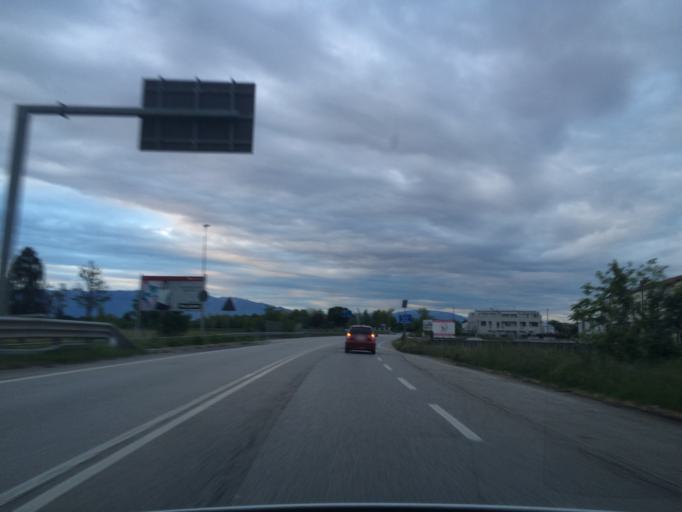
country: IT
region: Veneto
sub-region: Provincia di Padova
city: Cittadella
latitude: 45.6516
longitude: 11.7746
